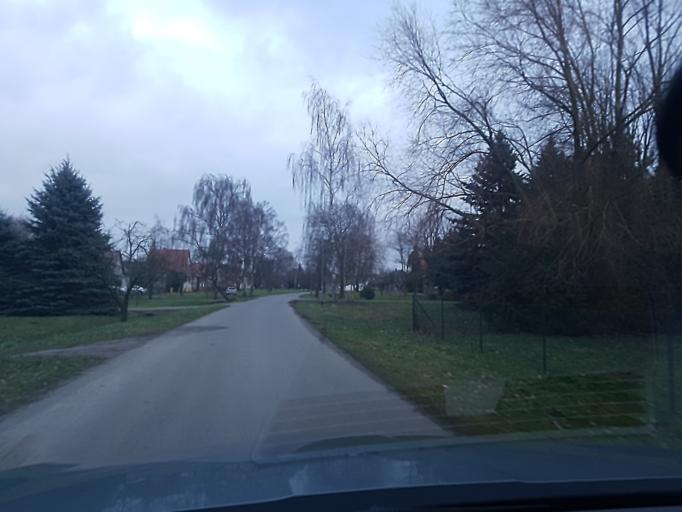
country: DE
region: Brandenburg
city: Schonewalde
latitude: 51.6808
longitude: 13.5985
